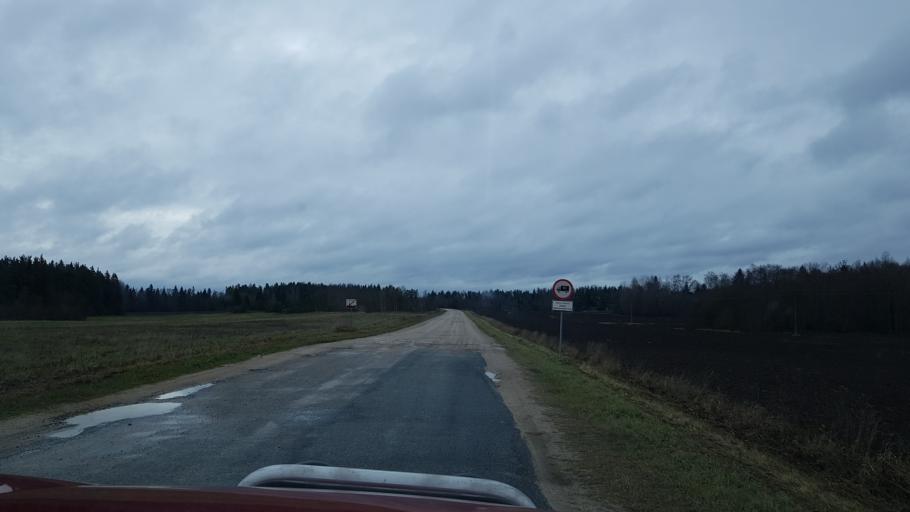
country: EE
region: Paernumaa
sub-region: Halinga vald
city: Parnu-Jaagupi
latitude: 58.5852
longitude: 24.4066
